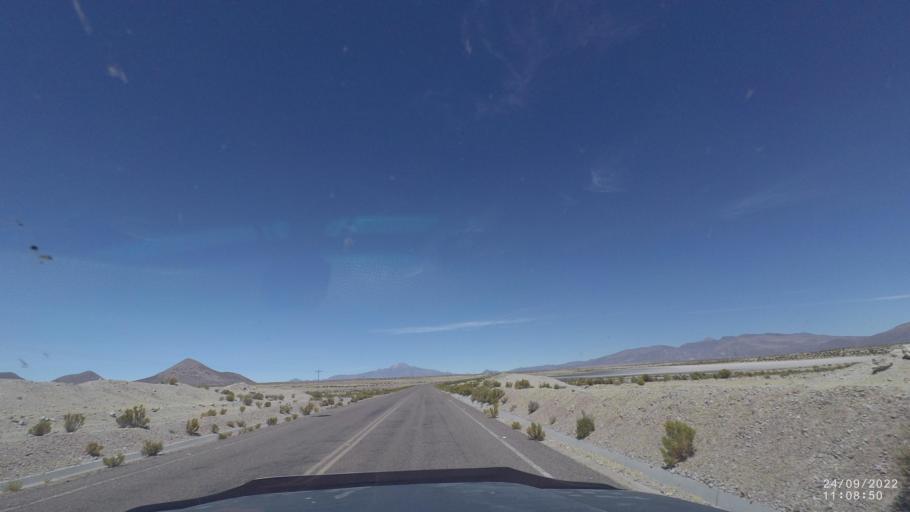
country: BO
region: Oruro
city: Challapata
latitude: -19.4893
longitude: -67.4453
